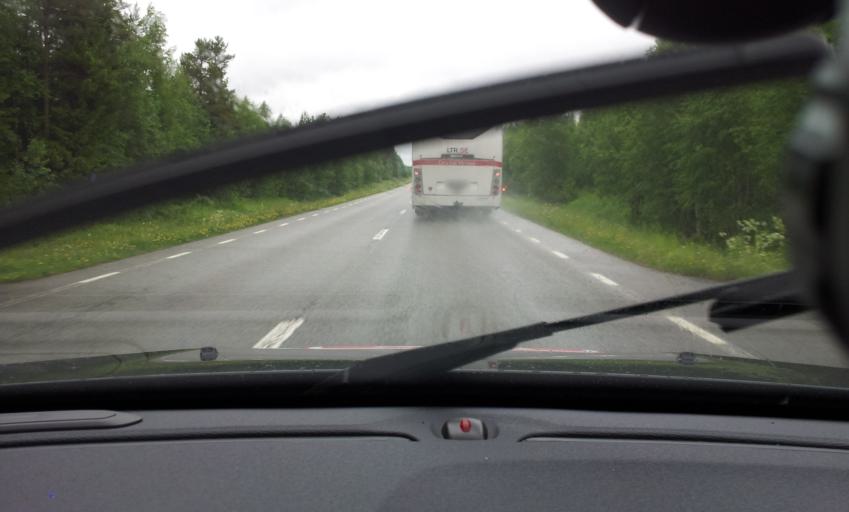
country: SE
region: Jaemtland
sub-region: OEstersunds Kommun
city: Lit
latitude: 63.5961
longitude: 14.6510
